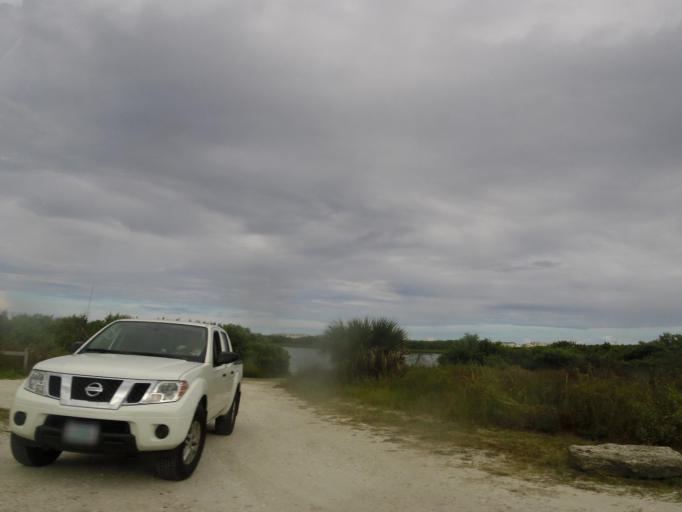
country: US
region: Florida
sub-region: Saint Johns County
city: Saint Augustine Beach
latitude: 29.8699
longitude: -81.2751
